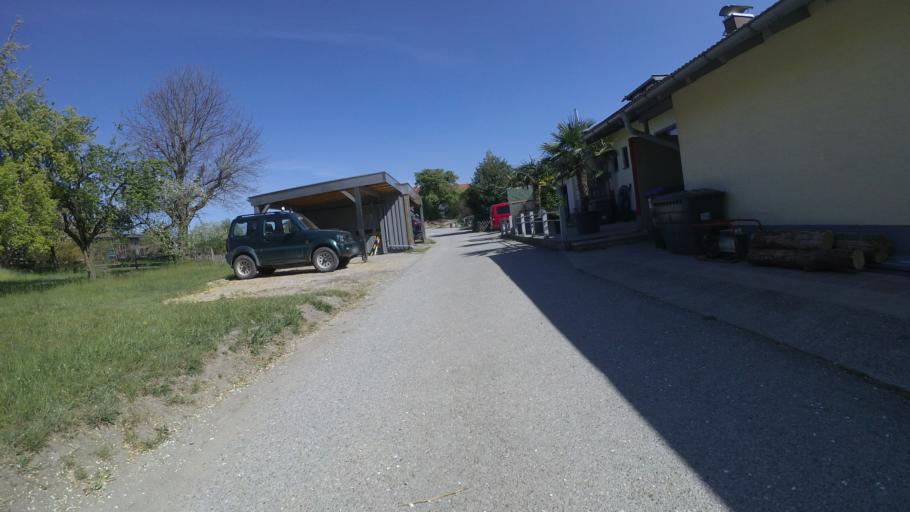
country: DE
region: Bavaria
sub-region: Upper Bavaria
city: Traunreut
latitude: 47.9454
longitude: 12.5441
